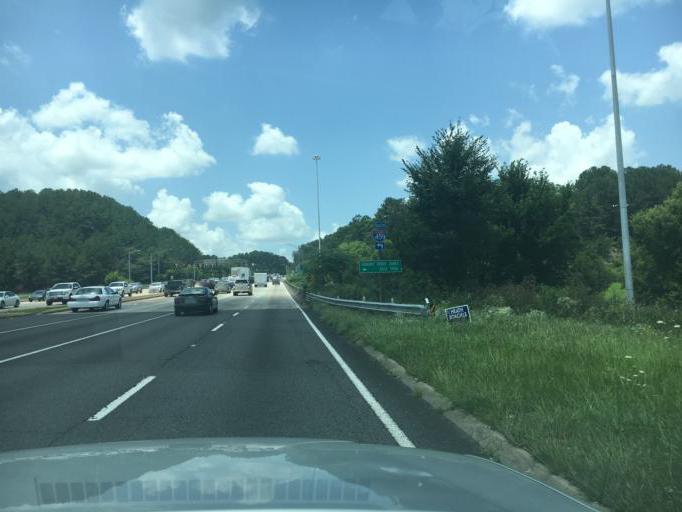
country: US
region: Alabama
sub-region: Jefferson County
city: Cahaba Heights
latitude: 33.4418
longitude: -86.7293
